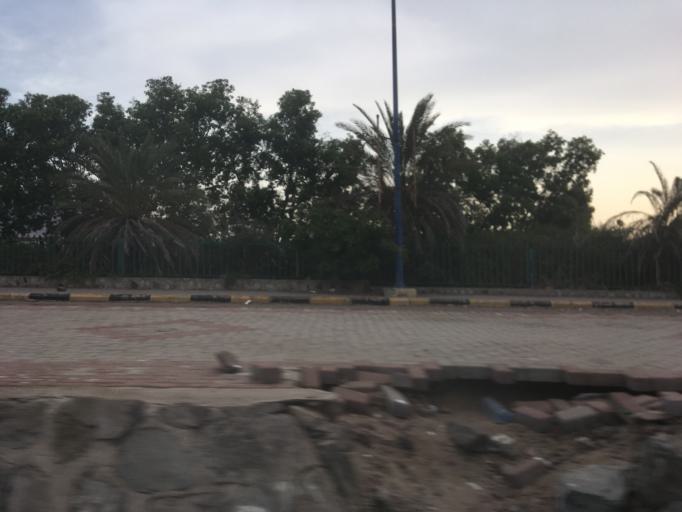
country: YE
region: Aden
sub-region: Khur Maksar
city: Khawr Maksar
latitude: 12.8065
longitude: 45.0270
